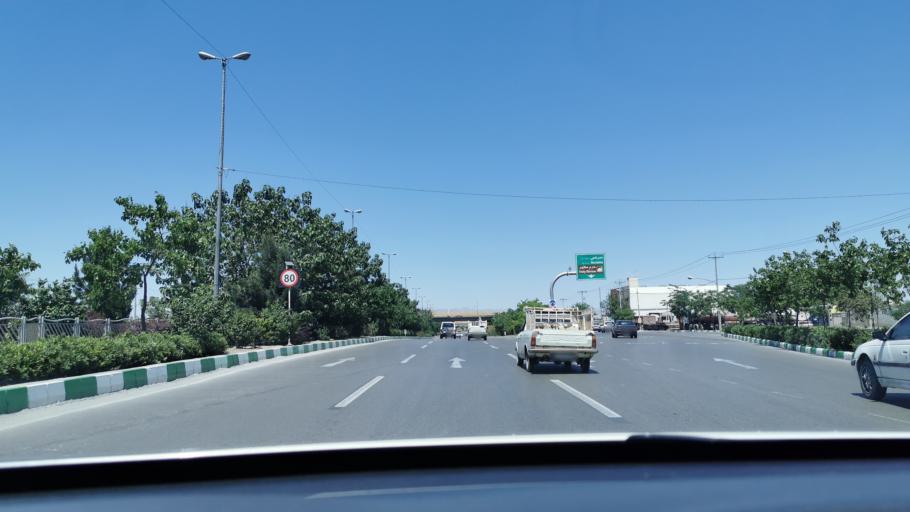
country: IR
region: Razavi Khorasan
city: Mashhad
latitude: 36.2648
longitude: 59.6529
